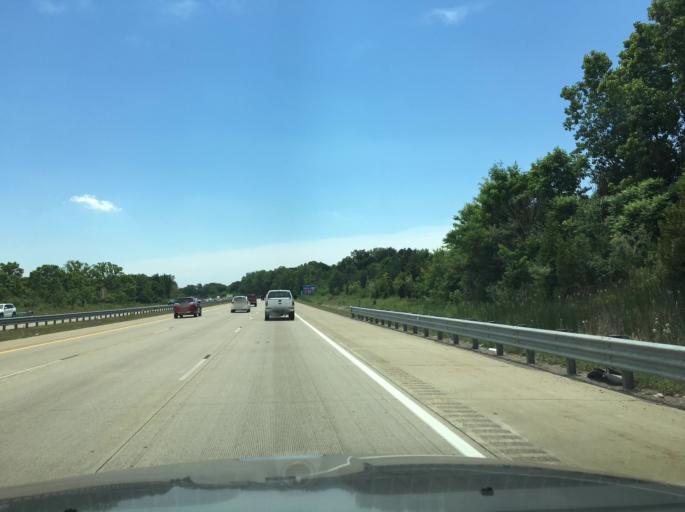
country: US
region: Michigan
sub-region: Oakland County
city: Rochester Hills
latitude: 42.6356
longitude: -83.1459
